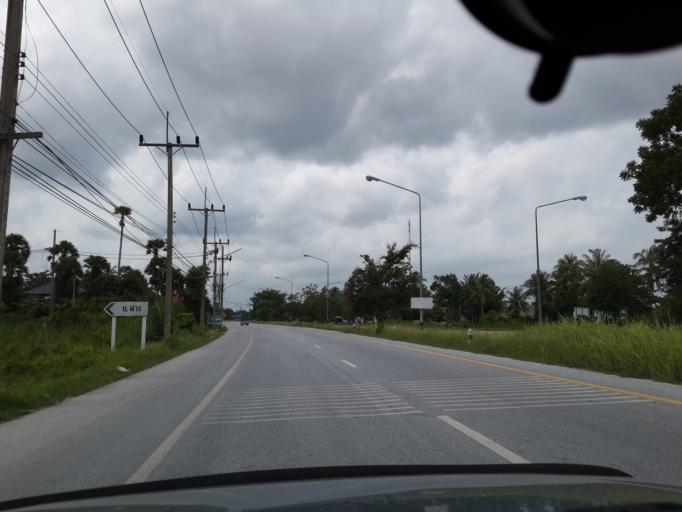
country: TH
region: Pattani
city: Yaring
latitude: 6.8696
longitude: 101.3509
